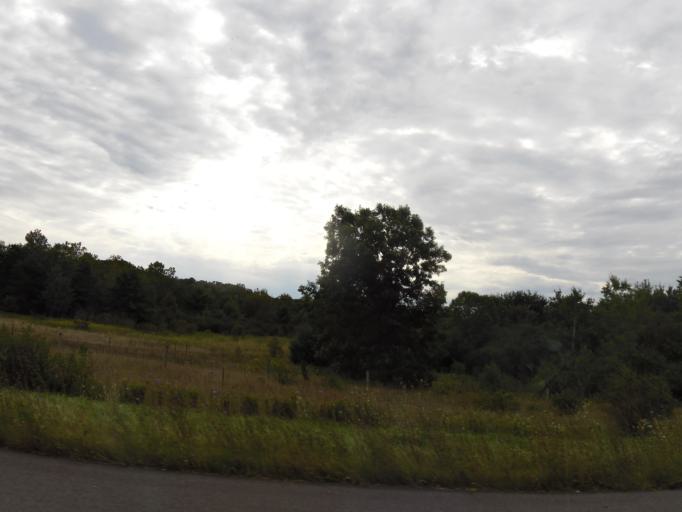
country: US
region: Wisconsin
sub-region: Monroe County
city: Tomah
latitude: 43.9641
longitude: -90.4903
